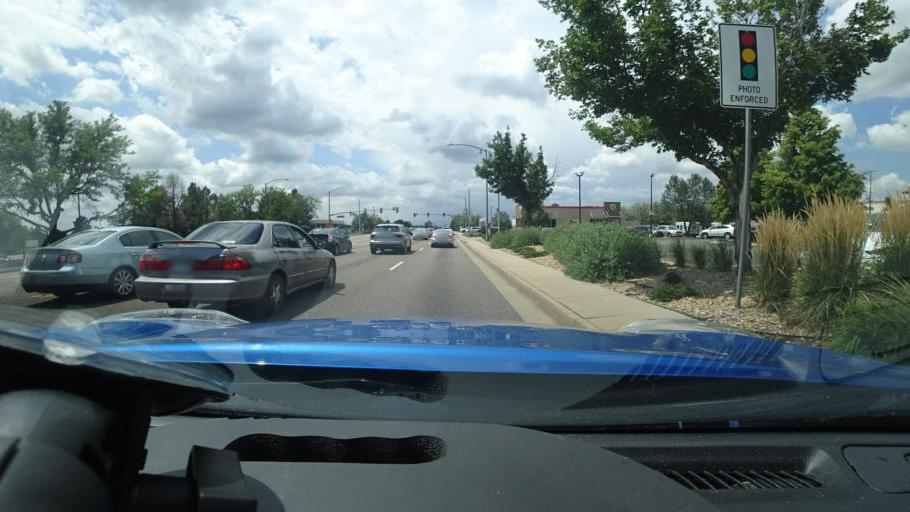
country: US
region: Colorado
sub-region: Adams County
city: Aurora
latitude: 39.6967
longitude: -104.8458
